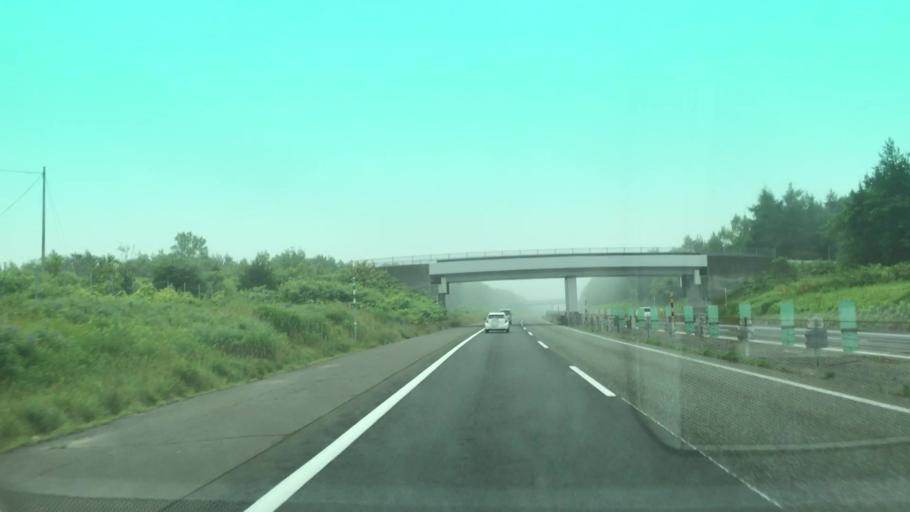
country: JP
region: Hokkaido
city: Chitose
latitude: 42.8274
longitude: 141.6142
